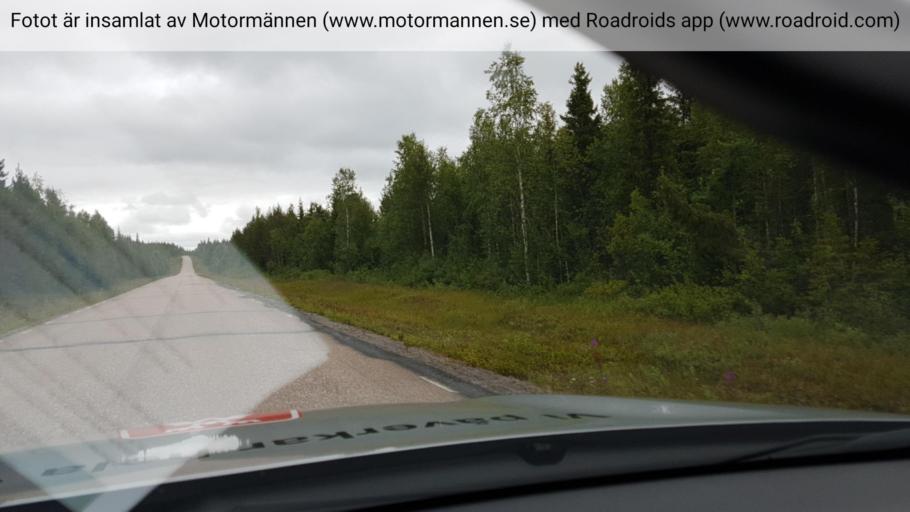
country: SE
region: Norrbotten
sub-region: Overkalix Kommun
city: OEverkalix
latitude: 67.0361
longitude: 22.0275
